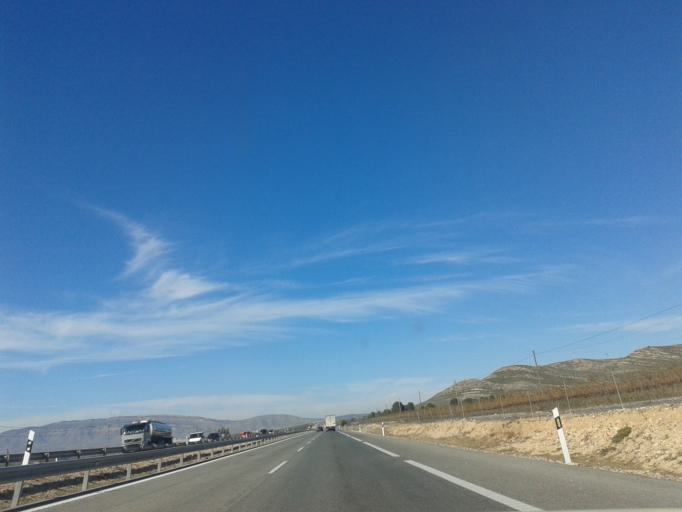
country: ES
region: Valencia
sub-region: Provincia de Alicante
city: Villena
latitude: 38.6842
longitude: -0.9021
